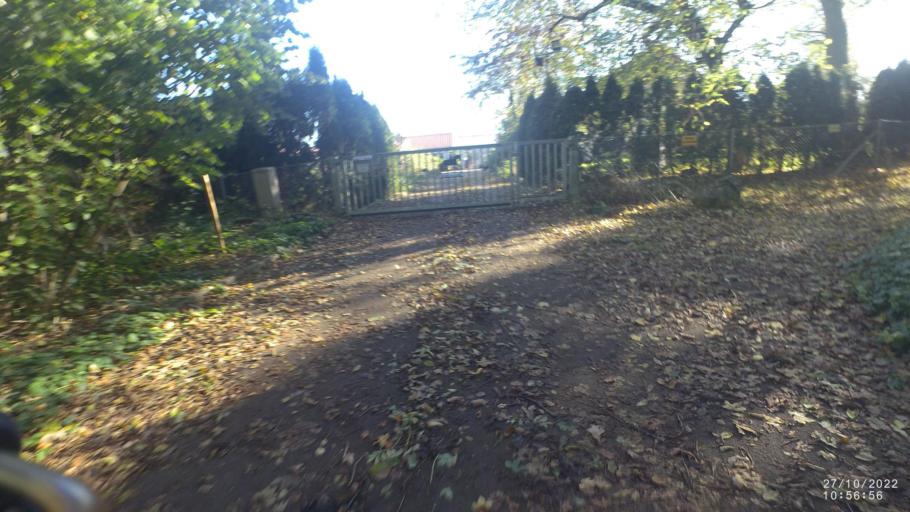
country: DE
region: Baden-Wuerttemberg
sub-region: Regierungsbezirk Stuttgart
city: Schlat
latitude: 48.6640
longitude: 9.6955
